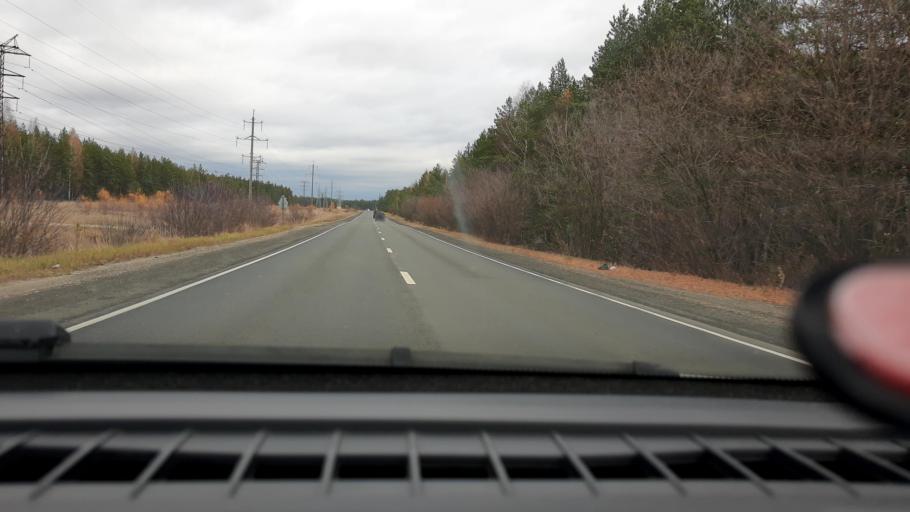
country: RU
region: Nizjnij Novgorod
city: Lukino
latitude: 56.3943
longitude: 43.6458
